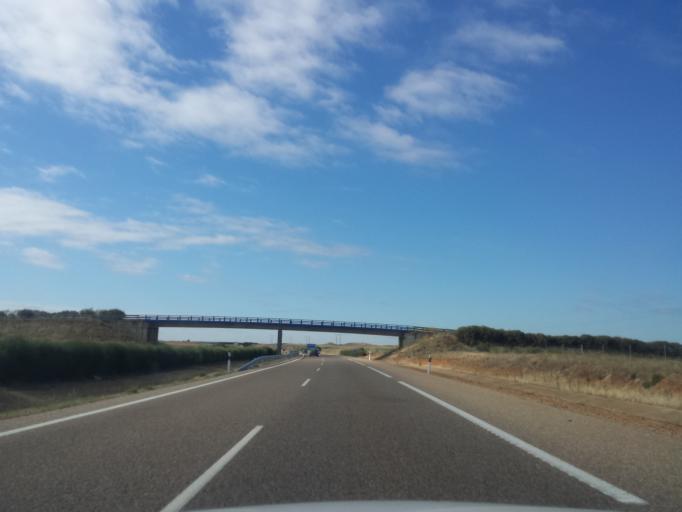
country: ES
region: Castille and Leon
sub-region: Provincia de Leon
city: Villademor de la Vega
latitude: 42.2594
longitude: -5.5943
